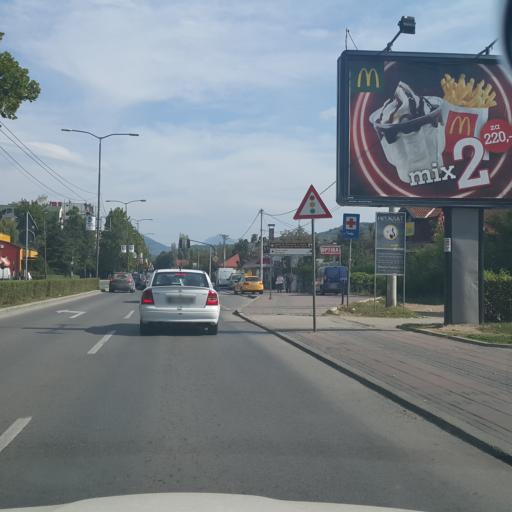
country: RS
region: Central Serbia
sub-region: Nisavski Okrug
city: Nis
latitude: 43.3158
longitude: 21.9155
